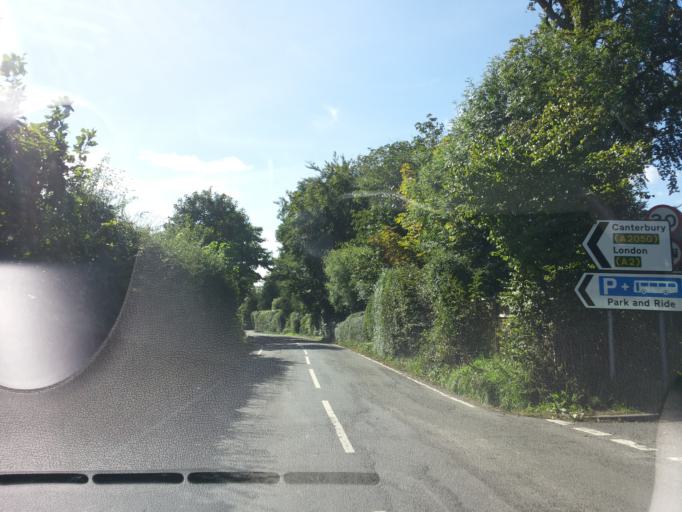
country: GB
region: England
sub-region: Kent
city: Sturry
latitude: 51.2522
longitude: 1.1216
